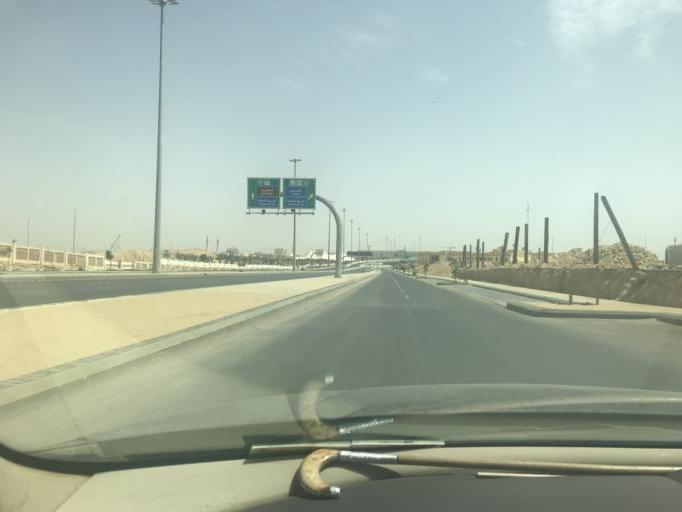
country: SA
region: Ar Riyad
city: Riyadh
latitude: 24.8253
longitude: 46.6970
